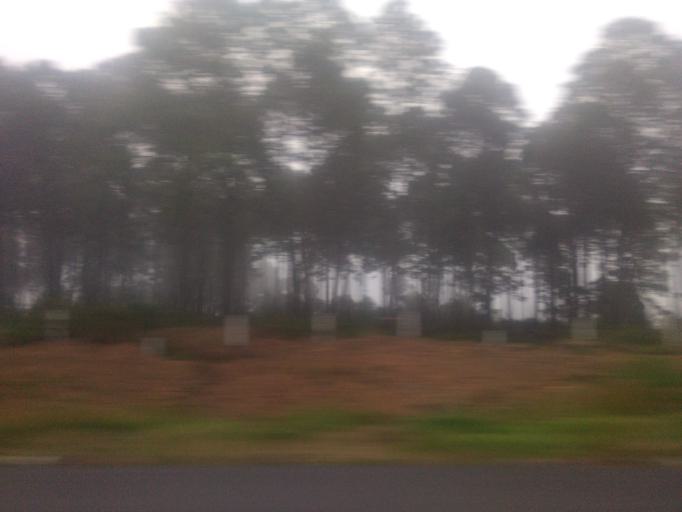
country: MX
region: Veracruz
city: Las Vigas
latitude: 19.6305
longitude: -97.1114
